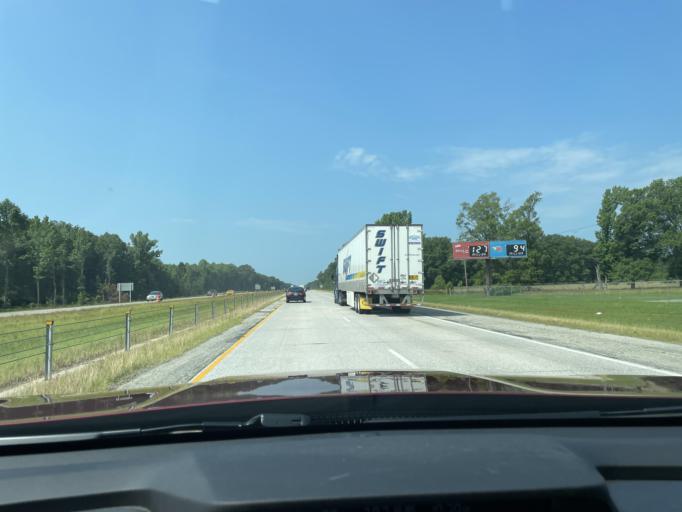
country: US
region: Arkansas
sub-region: White County
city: Searcy
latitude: 35.1932
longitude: -91.7446
